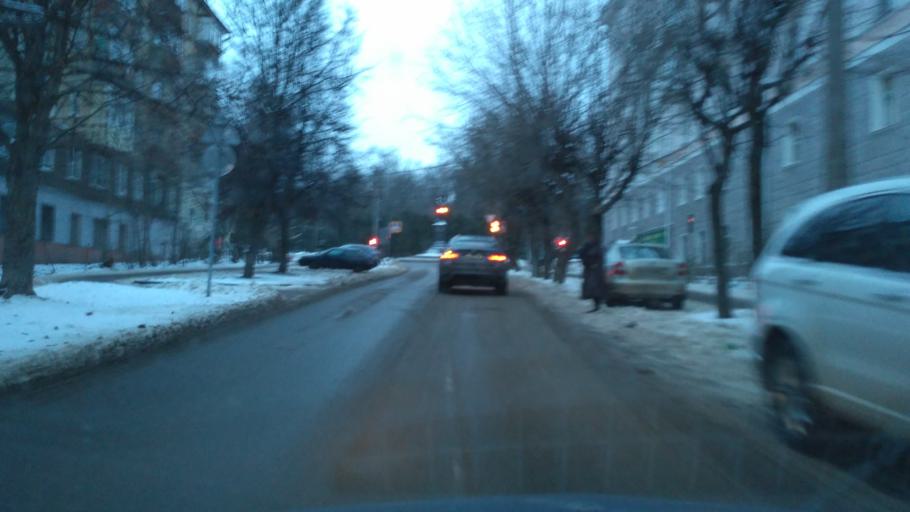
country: RU
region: Tula
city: Tula
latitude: 54.1847
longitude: 37.5980
